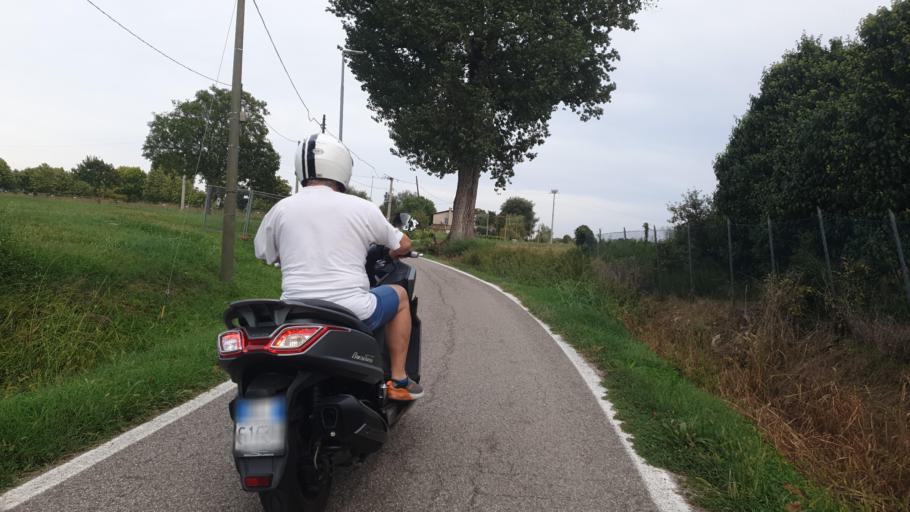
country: IT
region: Veneto
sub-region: Provincia di Padova
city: Albignasego
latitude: 45.3339
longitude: 11.8870
